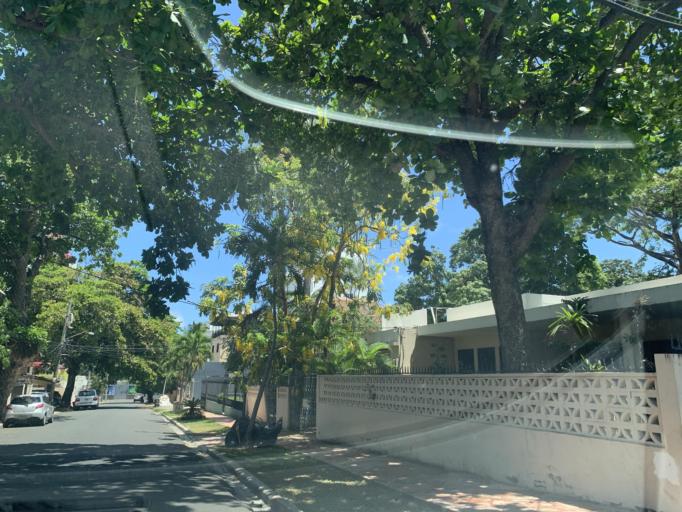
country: DO
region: Nacional
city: Ciudad Nueva
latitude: 18.4694
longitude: -69.9078
